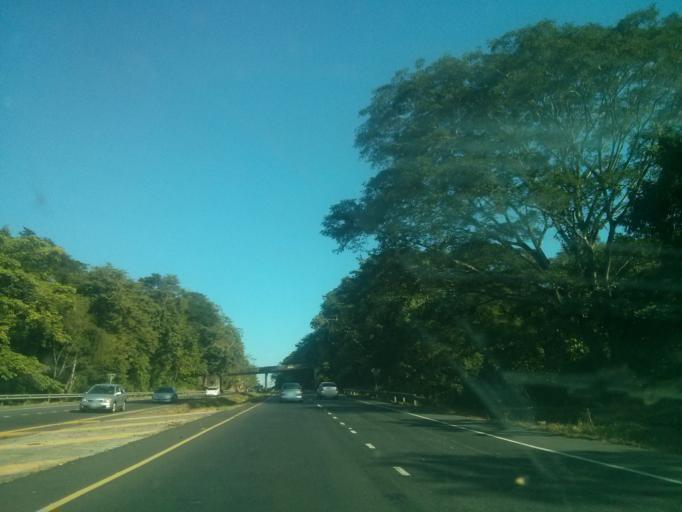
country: CR
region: Alajuela
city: Orotina
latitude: 9.9006
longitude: -84.5439
